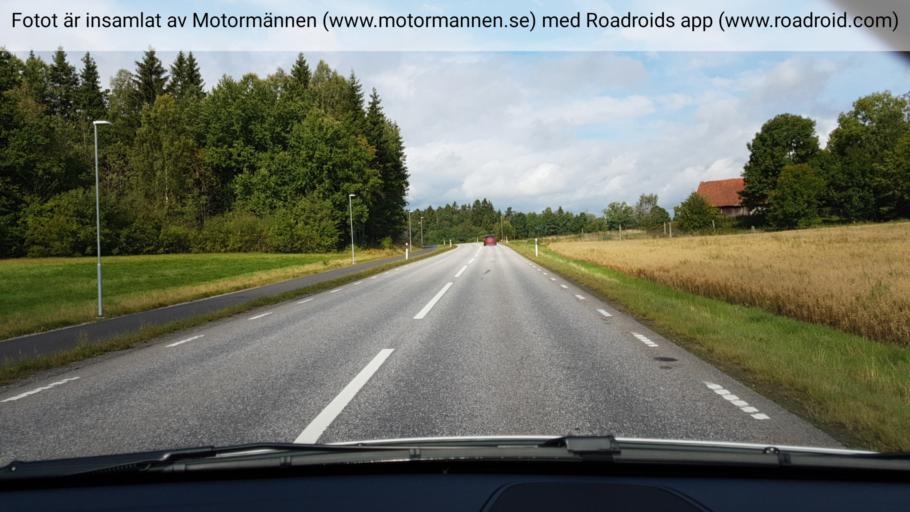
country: SE
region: Vaestra Goetaland
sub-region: Alingsas Kommun
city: Sollebrunn
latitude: 58.1108
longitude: 12.5793
